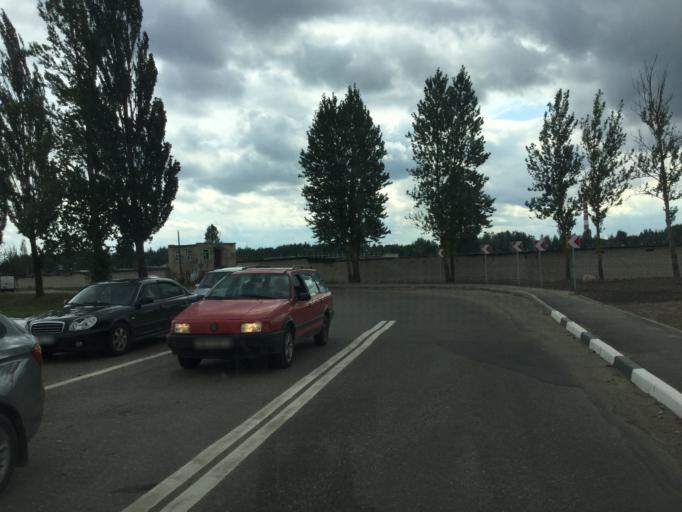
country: BY
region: Vitebsk
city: Vitebsk
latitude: 55.1661
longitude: 30.2550
